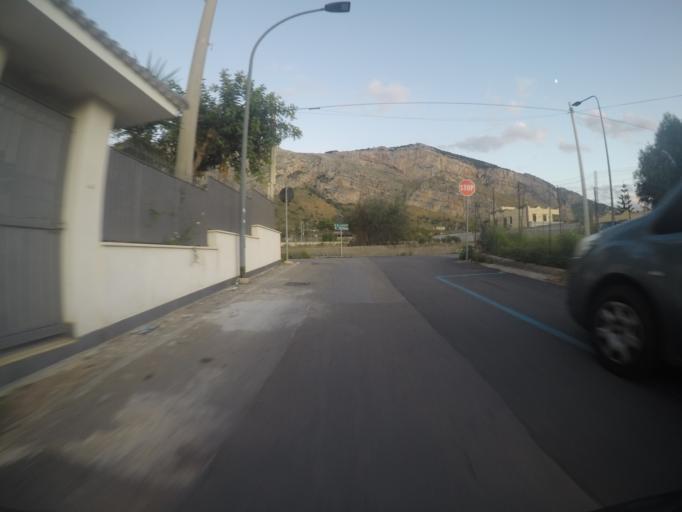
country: IT
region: Sicily
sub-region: Palermo
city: Isola delle Femmine
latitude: 38.1841
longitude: 13.2420
